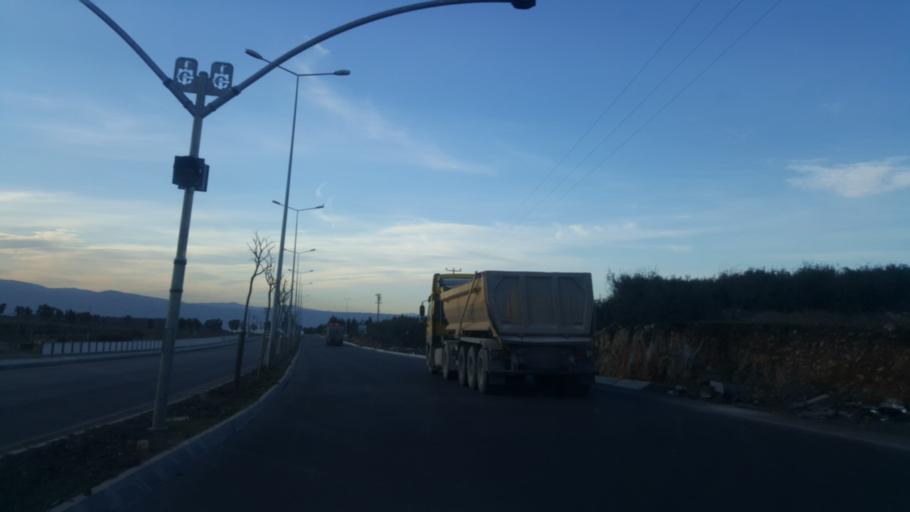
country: TR
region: Kocaeli
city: Tavsancil
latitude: 40.8033
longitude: 29.5513
